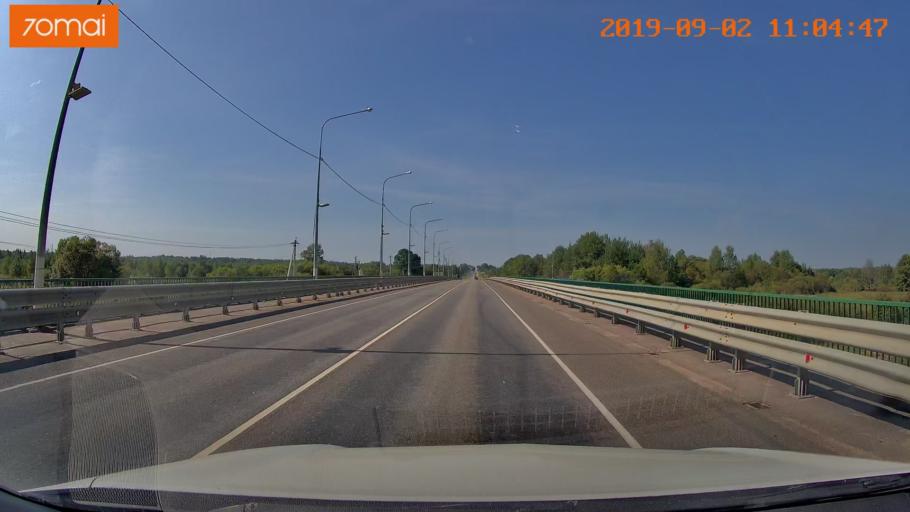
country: RU
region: Smolensk
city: Yekimovichi
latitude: 54.1243
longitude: 33.3264
